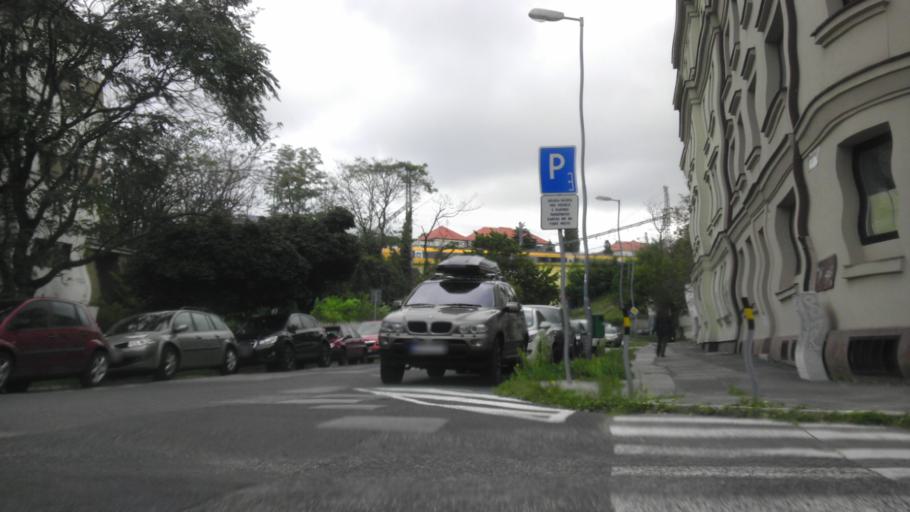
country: SK
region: Bratislavsky
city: Bratislava
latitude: 48.1572
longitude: 17.1082
